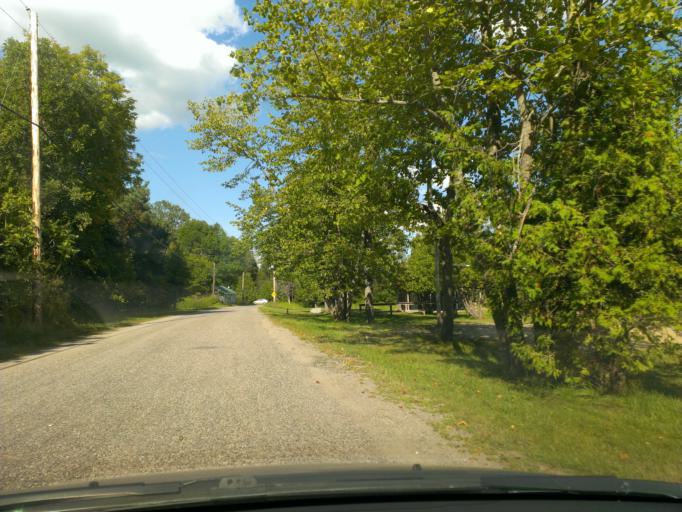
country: CA
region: Ontario
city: Skatepark
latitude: 44.7412
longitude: -76.9045
